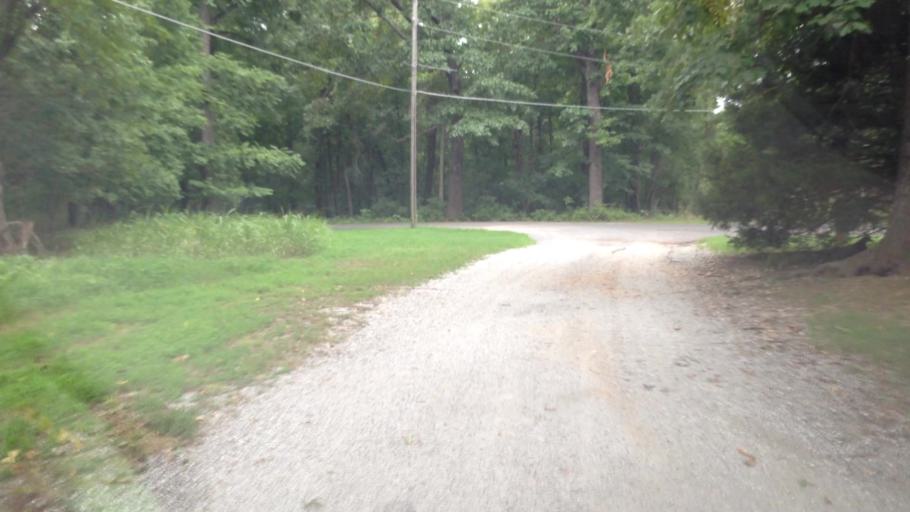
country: US
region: Oklahoma
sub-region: Delaware County
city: Cleora
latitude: 36.5487
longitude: -94.9663
